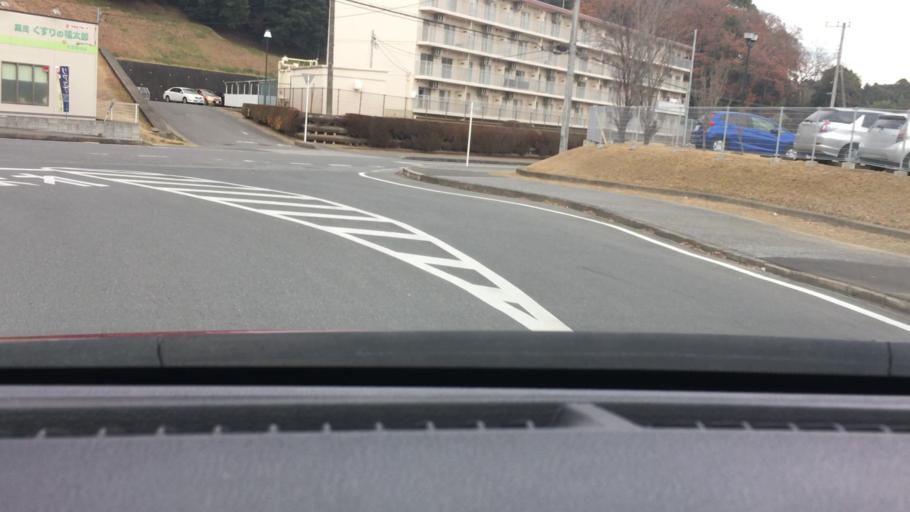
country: JP
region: Chiba
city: Ichihara
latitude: 35.4668
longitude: 140.0634
